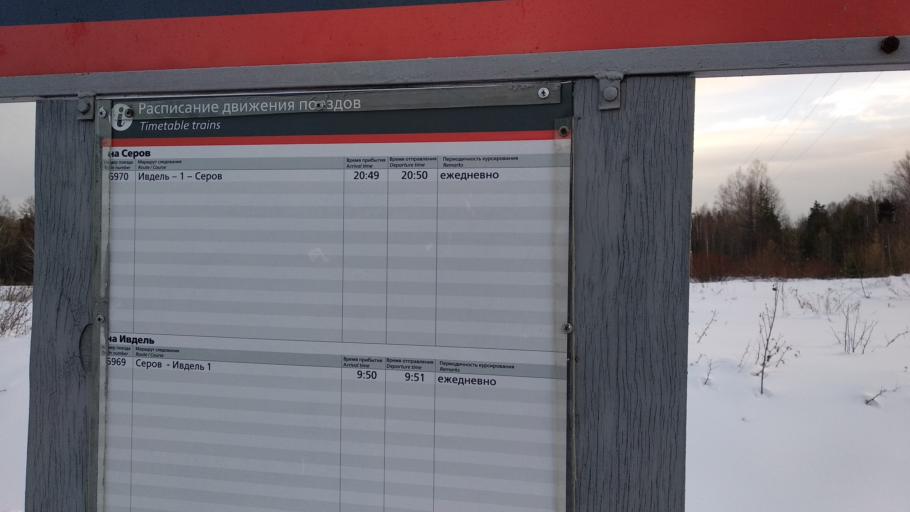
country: RU
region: Sverdlovsk
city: Serov
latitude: 59.8484
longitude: 60.6389
